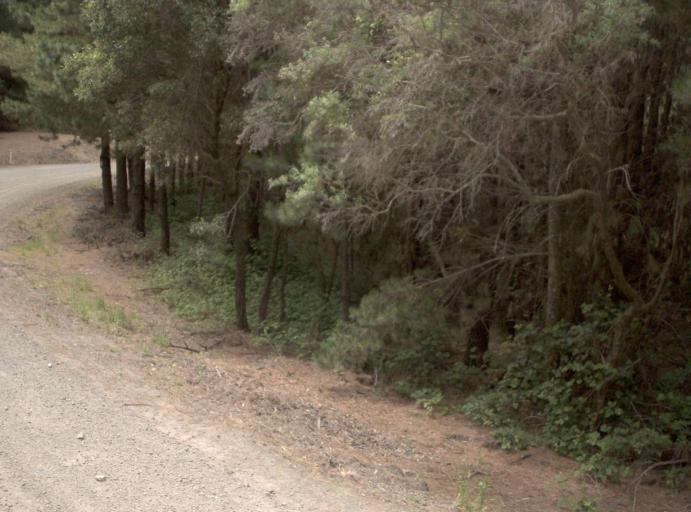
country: AU
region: Victoria
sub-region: Latrobe
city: Traralgon
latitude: -38.3857
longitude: 146.6634
